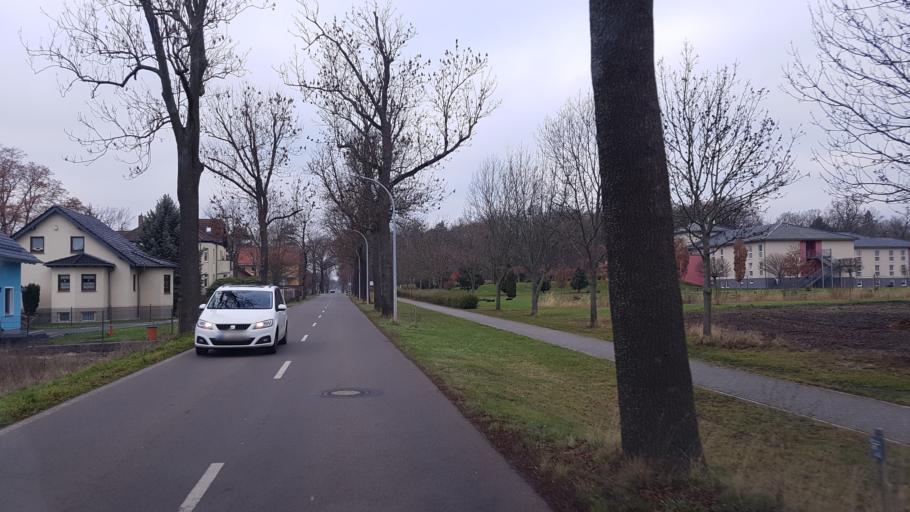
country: DE
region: Brandenburg
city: Schipkau
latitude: 51.5601
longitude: 13.8875
